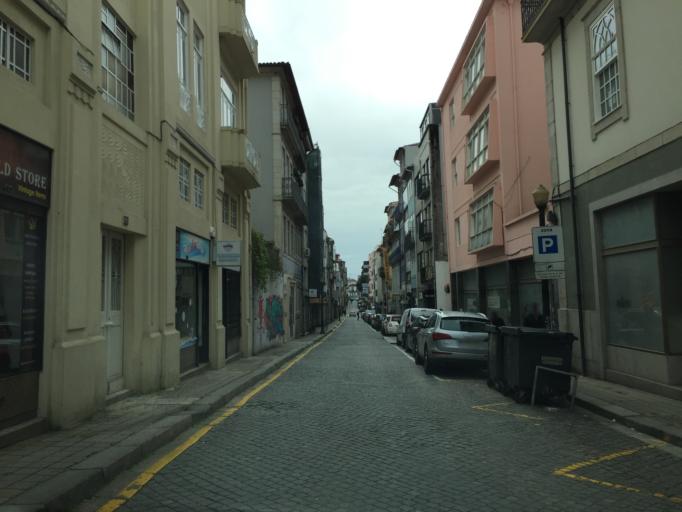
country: PT
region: Porto
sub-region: Porto
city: Porto
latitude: 41.1494
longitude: -8.6041
